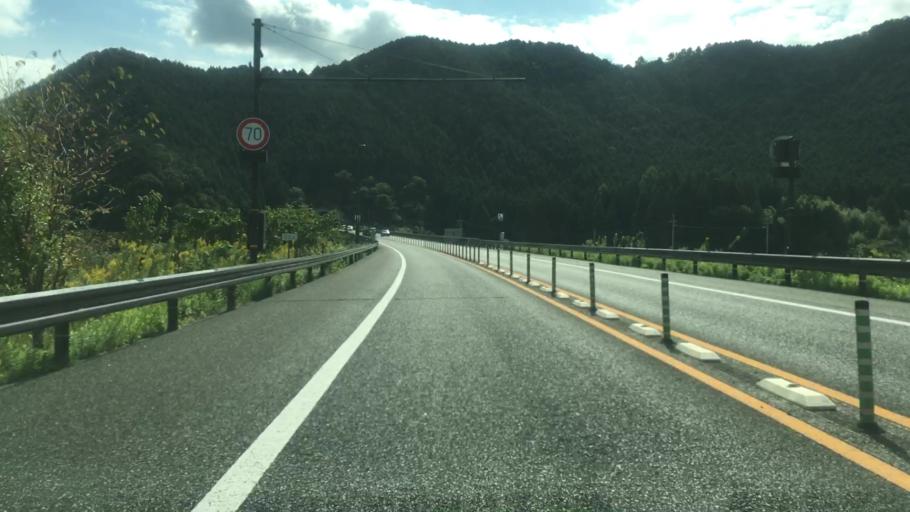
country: JP
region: Kyoto
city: Fukuchiyama
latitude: 35.2311
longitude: 135.0227
